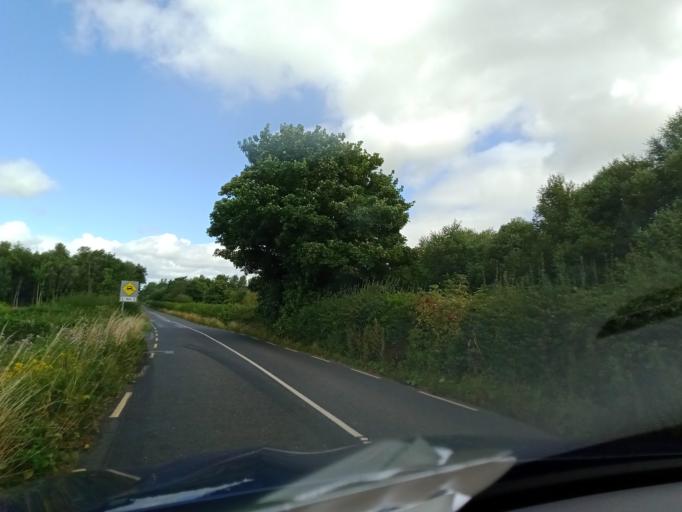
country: IE
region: Leinster
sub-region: Laois
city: Portlaoise
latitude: 52.9814
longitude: -7.2887
